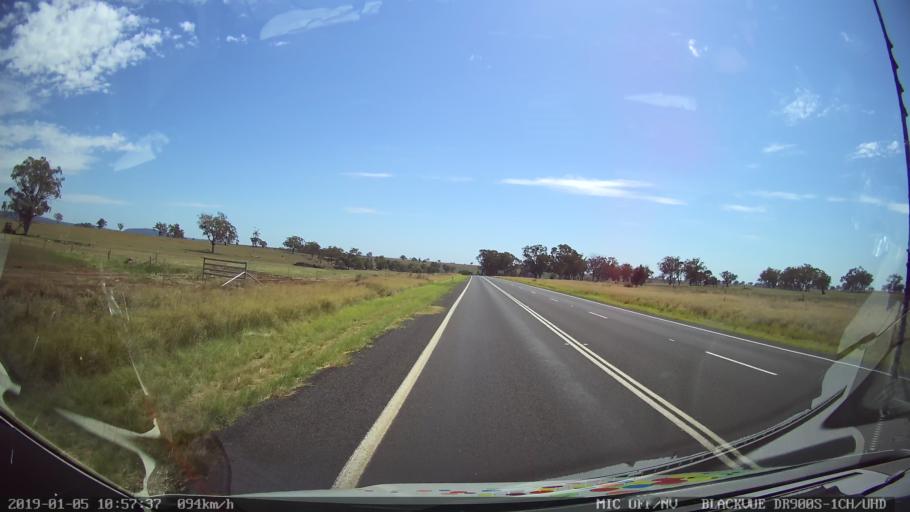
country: AU
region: New South Wales
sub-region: Warrumbungle Shire
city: Coonabarabran
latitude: -31.4297
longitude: 149.1721
